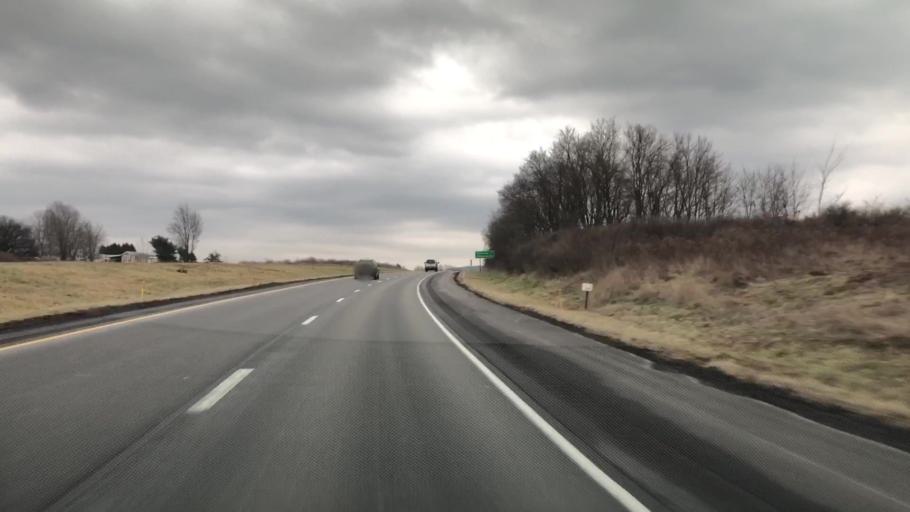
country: US
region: Pennsylvania
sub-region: Butler County
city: Slippery Rock
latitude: 41.0328
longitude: -80.1206
